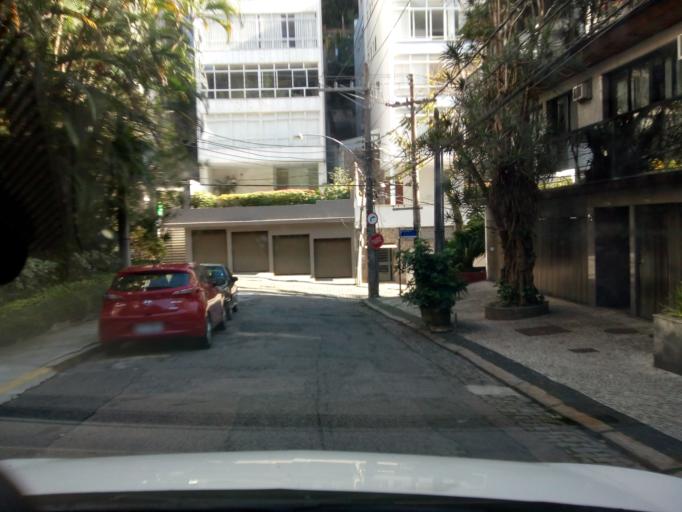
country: BR
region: Rio de Janeiro
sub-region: Rio De Janeiro
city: Rio de Janeiro
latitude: -22.9869
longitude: -43.2325
